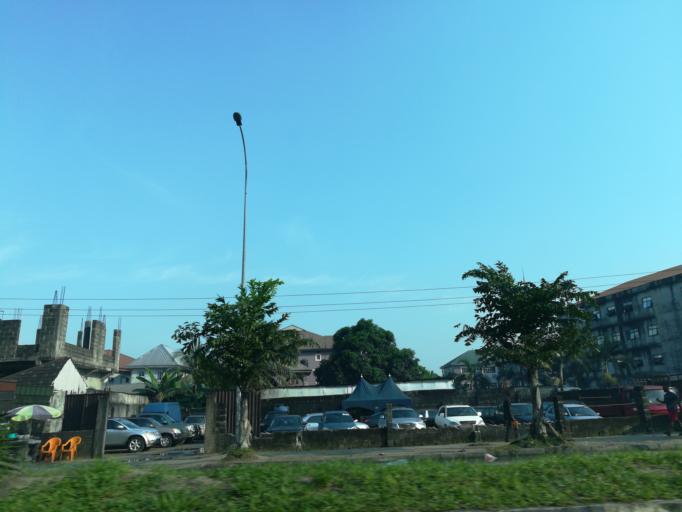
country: NG
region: Rivers
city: Port Harcourt
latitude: 4.8220
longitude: 7.0200
